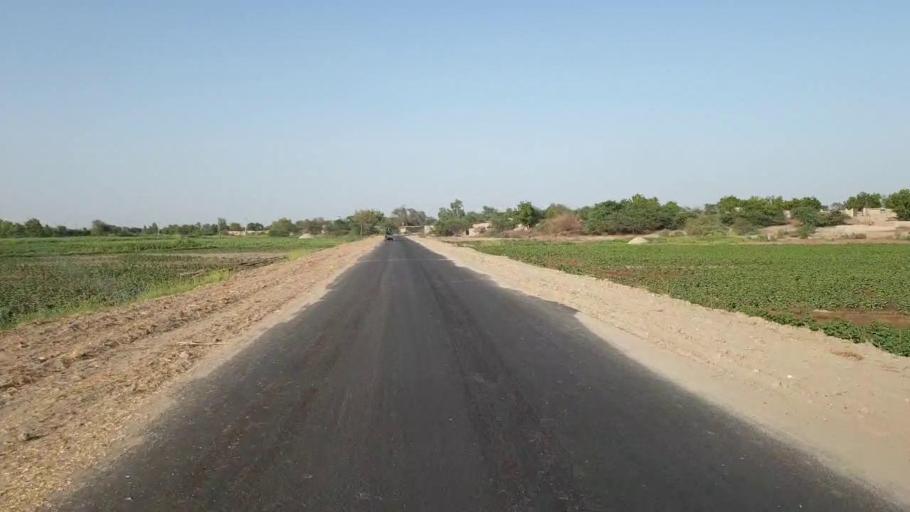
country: PK
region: Sindh
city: Jam Sahib
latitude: 26.3479
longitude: 68.5602
